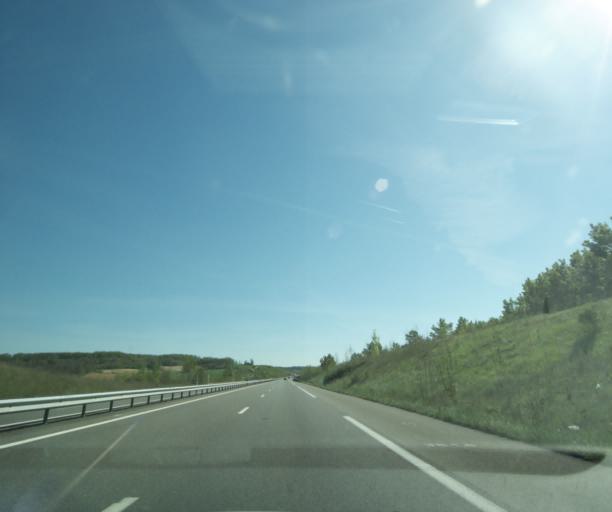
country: FR
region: Midi-Pyrenees
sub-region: Departement du Lot
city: Lalbenque
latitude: 44.2755
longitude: 1.5051
